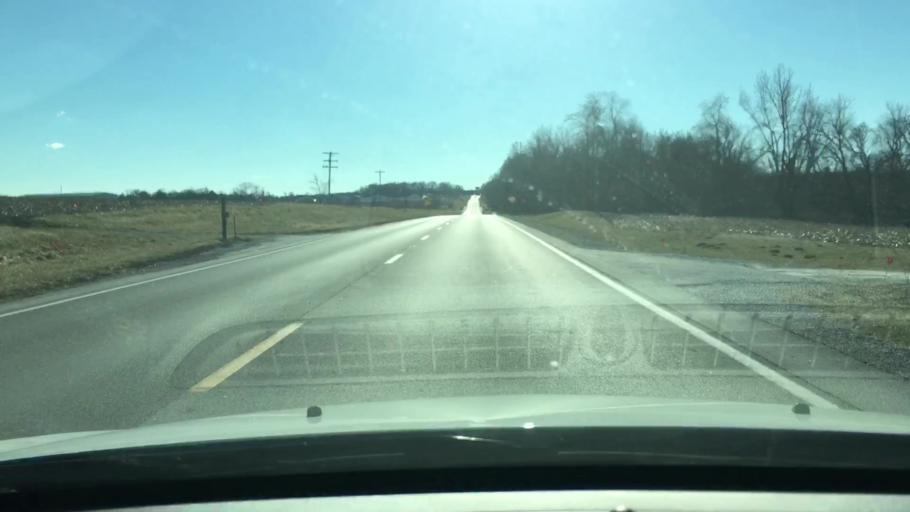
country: US
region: Illinois
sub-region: Pike County
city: Pittsfield
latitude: 39.6431
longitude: -90.7854
